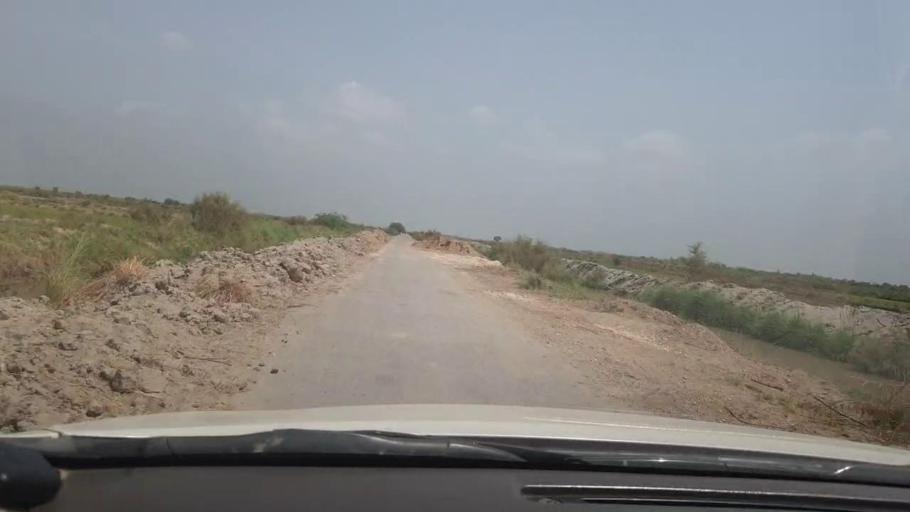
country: PK
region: Sindh
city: Garhi Yasin
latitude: 28.0114
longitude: 68.4994
